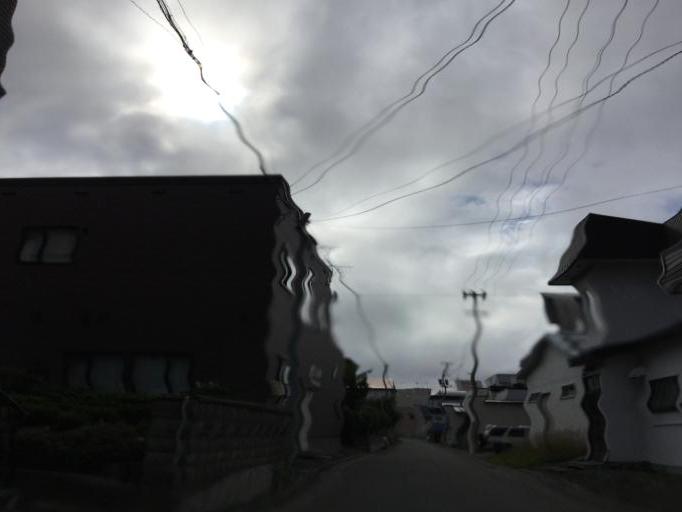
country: JP
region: Hokkaido
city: Wakkanai
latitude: 45.3988
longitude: 141.6886
